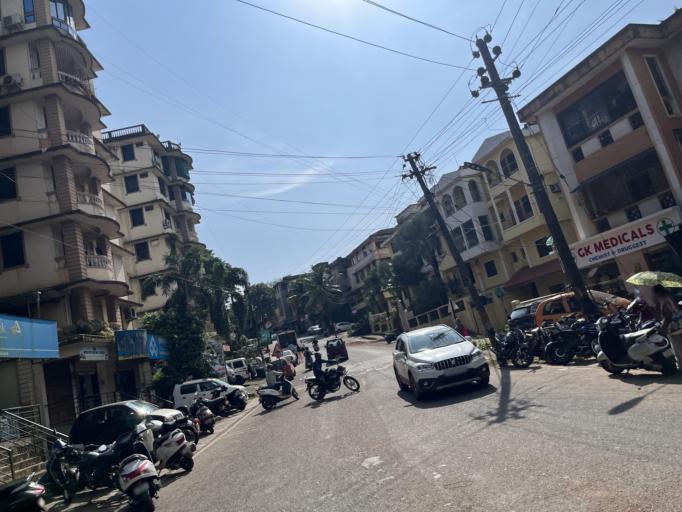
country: IN
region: Goa
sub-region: North Goa
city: Ponda
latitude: 15.4003
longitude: 74.0104
